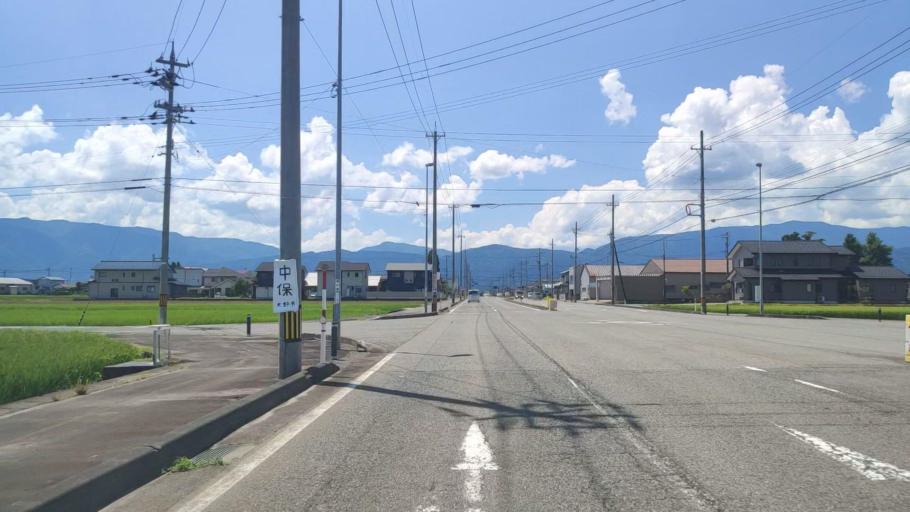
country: JP
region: Fukui
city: Ono
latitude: 35.9909
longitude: 136.5099
